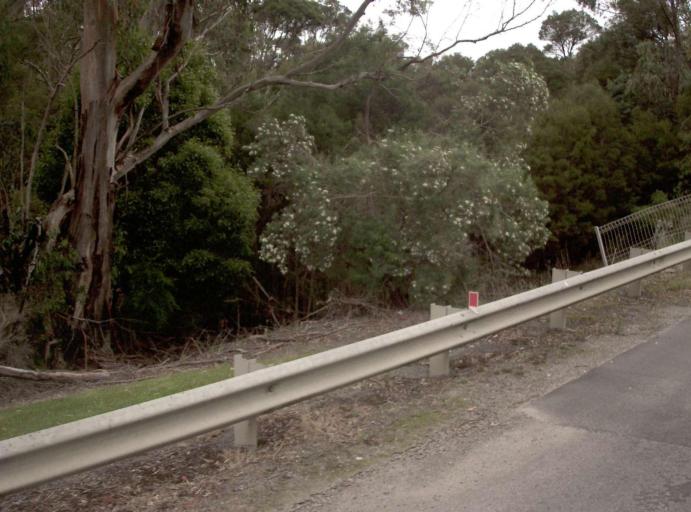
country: AU
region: Victoria
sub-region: Bass Coast
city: North Wonthaggi
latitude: -38.5428
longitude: 145.9474
